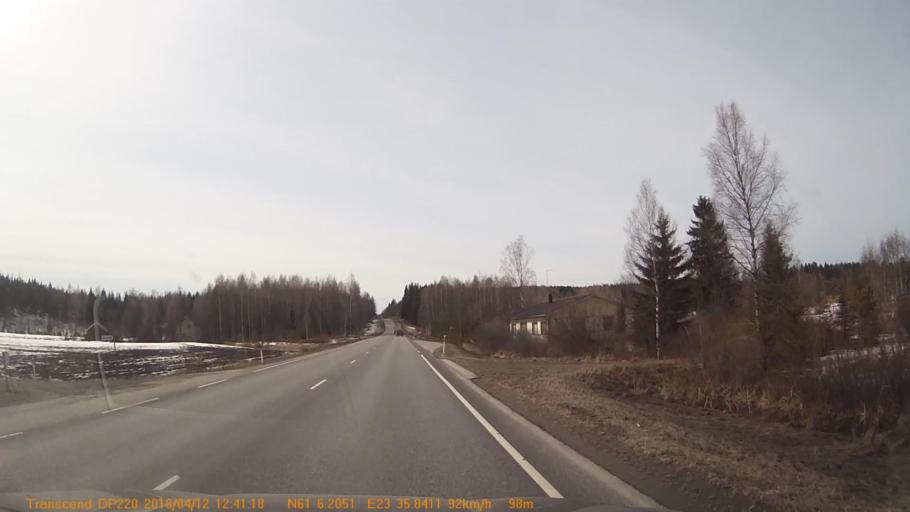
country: FI
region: Pirkanmaa
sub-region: Etelae-Pirkanmaa
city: Urjala
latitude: 61.1033
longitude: 23.5968
